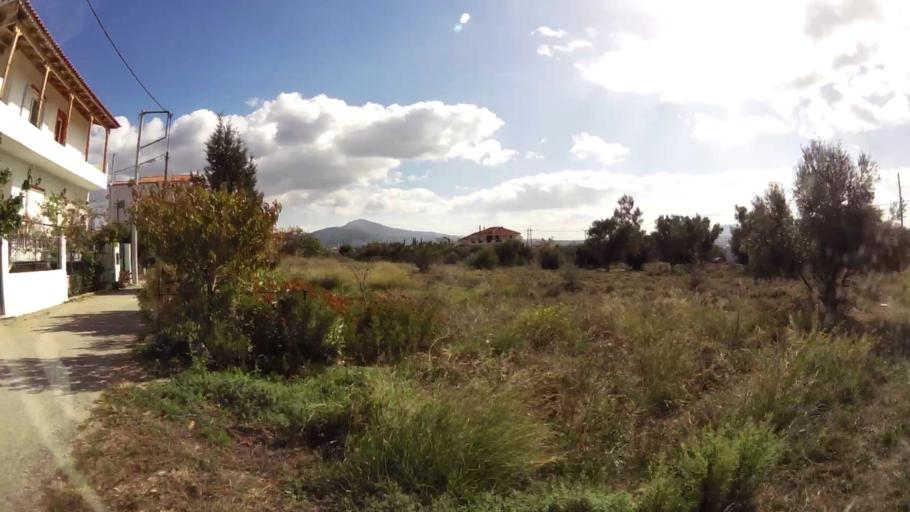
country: GR
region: Attica
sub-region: Nomarchia Anatolikis Attikis
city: Thrakomakedones
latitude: 38.1172
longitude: 23.7504
